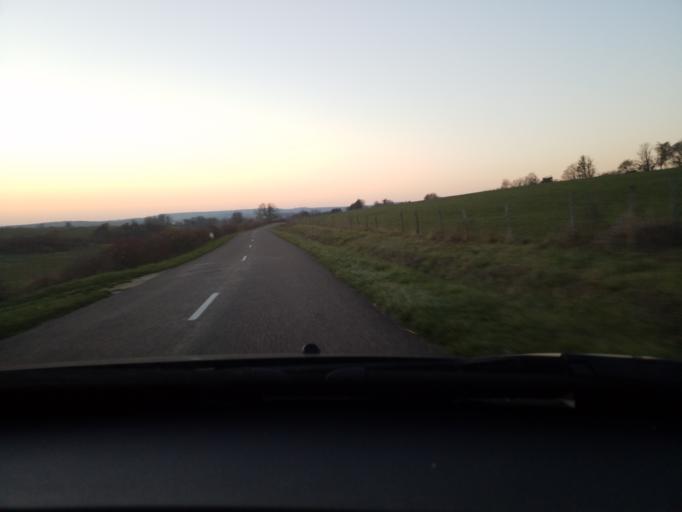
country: FR
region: Franche-Comte
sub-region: Departement de la Haute-Saone
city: Faverney
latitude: 47.8828
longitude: 6.1429
